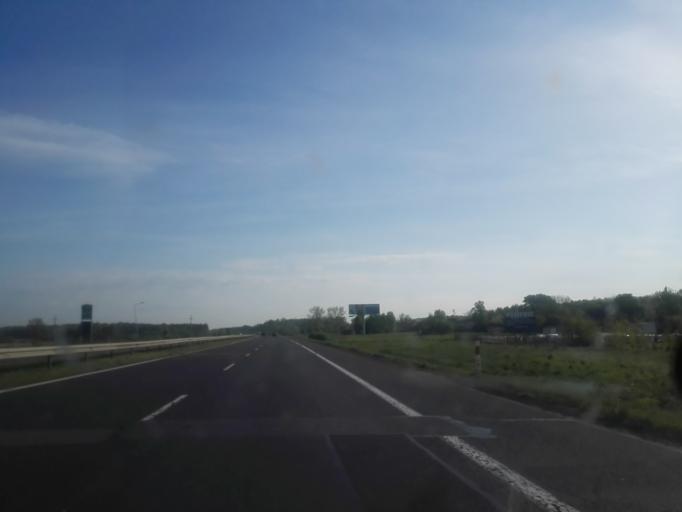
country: PL
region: Lodz Voivodeship
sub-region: Powiat radomszczanski
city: Kamiensk
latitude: 51.2333
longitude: 19.5146
